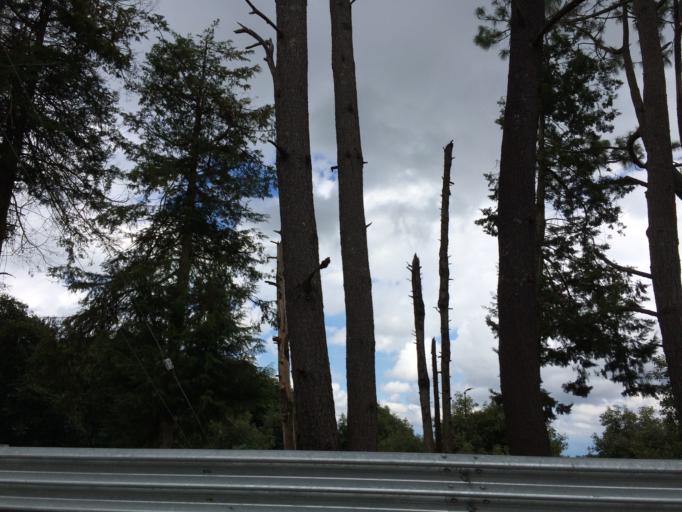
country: MX
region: Michoacan
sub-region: Uruapan
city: Santa Ana Zirosto
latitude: 19.5505
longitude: -102.3149
